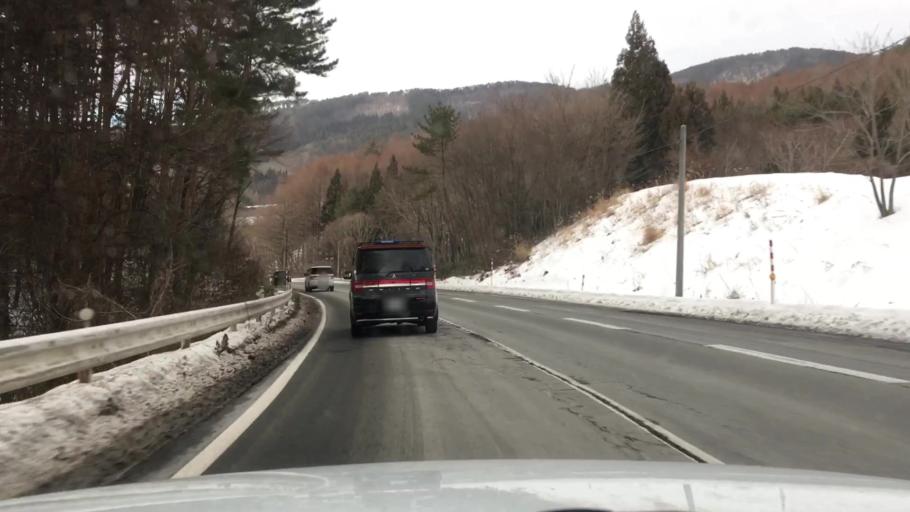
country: JP
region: Iwate
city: Morioka-shi
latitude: 39.6667
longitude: 141.3323
